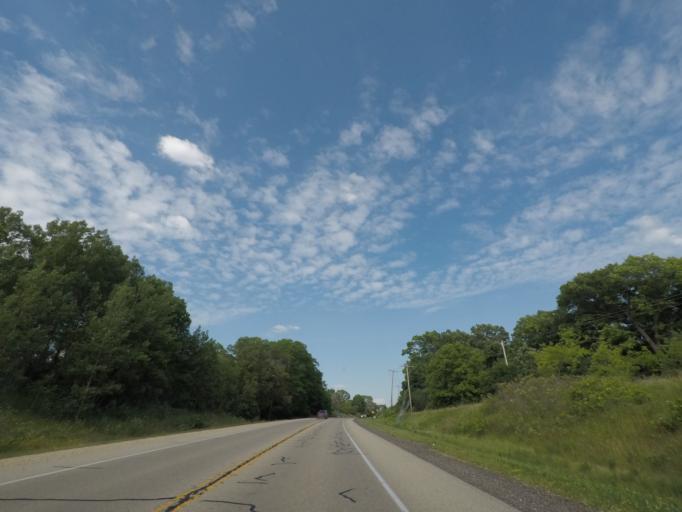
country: US
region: Wisconsin
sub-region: Jefferson County
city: Palmyra
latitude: 42.7975
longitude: -88.6120
